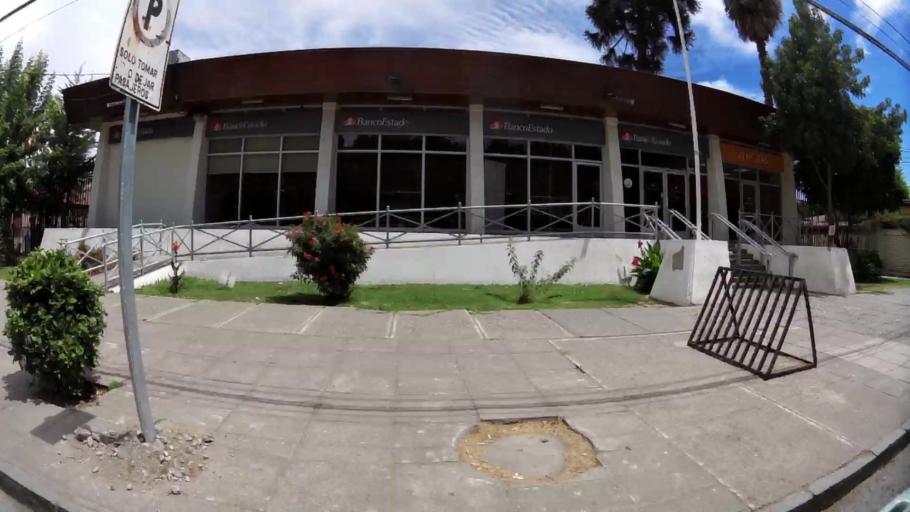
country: CL
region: O'Higgins
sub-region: Provincia de Cachapoal
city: Graneros
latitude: -34.0644
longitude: -70.7271
